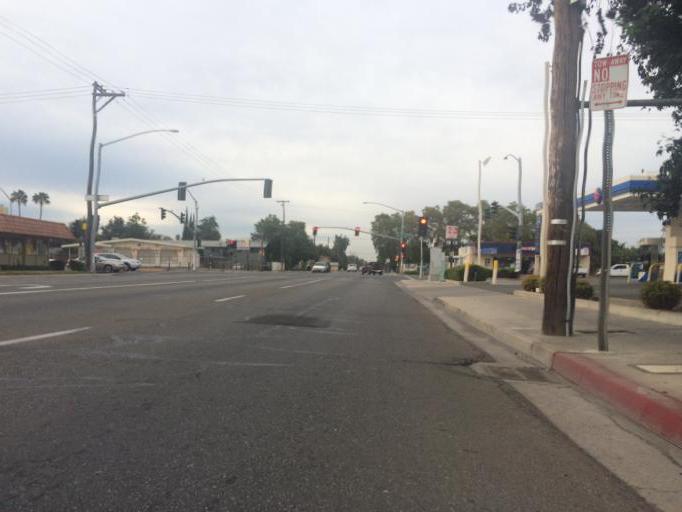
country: US
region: California
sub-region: Fresno County
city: Fresno
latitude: 36.7510
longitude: -119.7455
